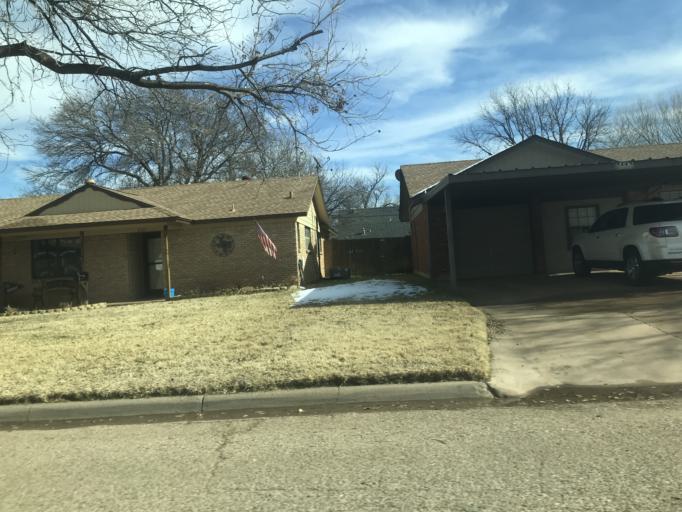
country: US
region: Texas
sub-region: Taylor County
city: Abilene
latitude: 32.4735
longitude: -99.7702
